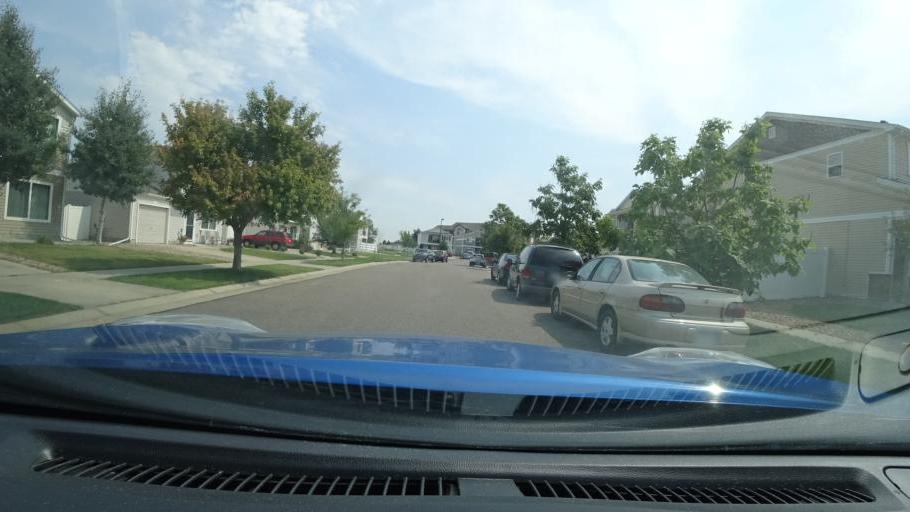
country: US
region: Colorado
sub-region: Adams County
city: Aurora
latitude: 39.7814
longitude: -104.7695
